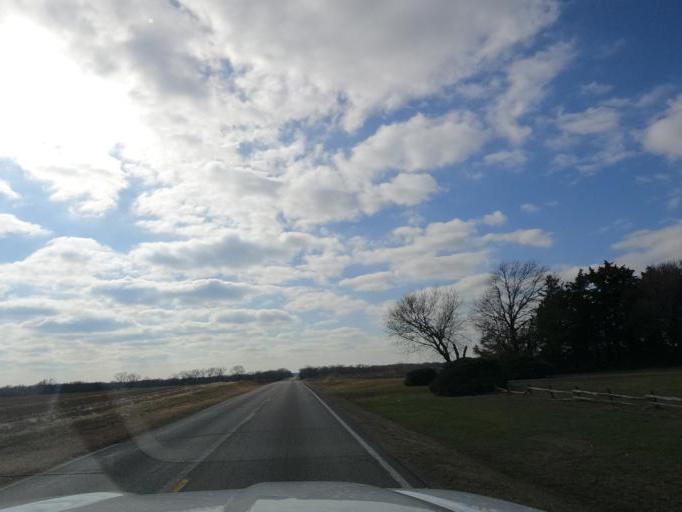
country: US
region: Kansas
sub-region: McPherson County
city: Inman
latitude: 38.2321
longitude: -97.8684
